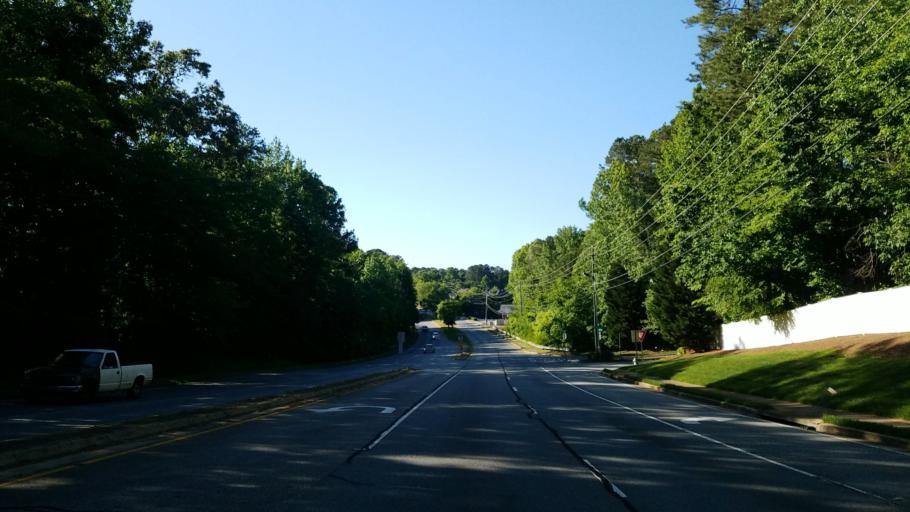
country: US
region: Georgia
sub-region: Cherokee County
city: Woodstock
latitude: 34.0732
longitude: -84.5706
